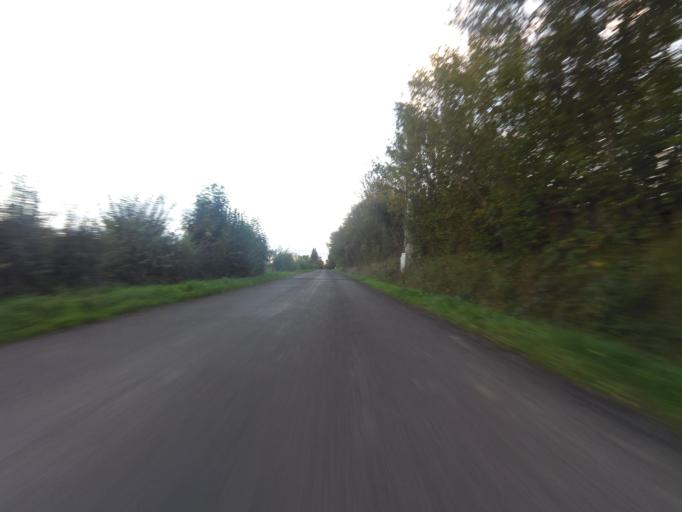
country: FR
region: Lower Normandy
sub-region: Departement de l'Orne
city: Vimoutiers
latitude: 48.9207
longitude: 0.2640
